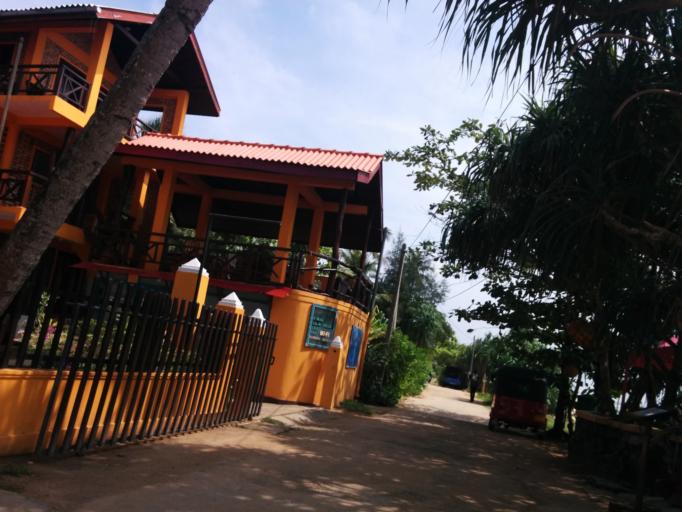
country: LK
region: Southern
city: Tangalla
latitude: 6.0363
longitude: 80.8044
